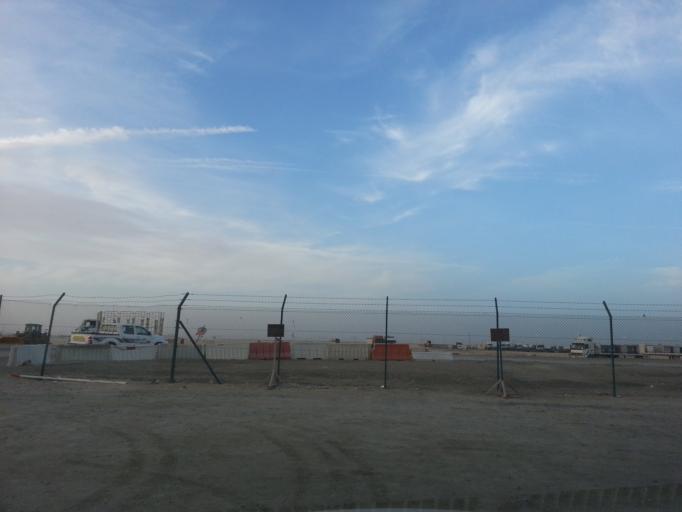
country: AE
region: Abu Dhabi
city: Abu Dhabi
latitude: 24.7787
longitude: 54.7316
